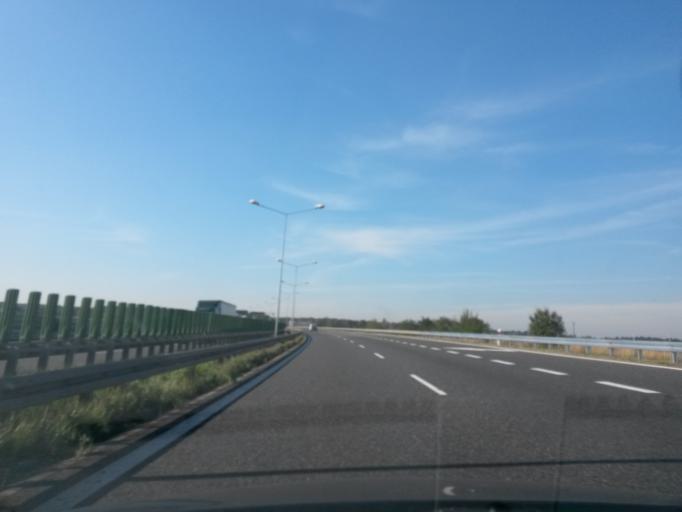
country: PL
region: Silesian Voivodeship
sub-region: Powiat gliwicki
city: Sosnicowice
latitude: 50.3472
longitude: 18.5387
